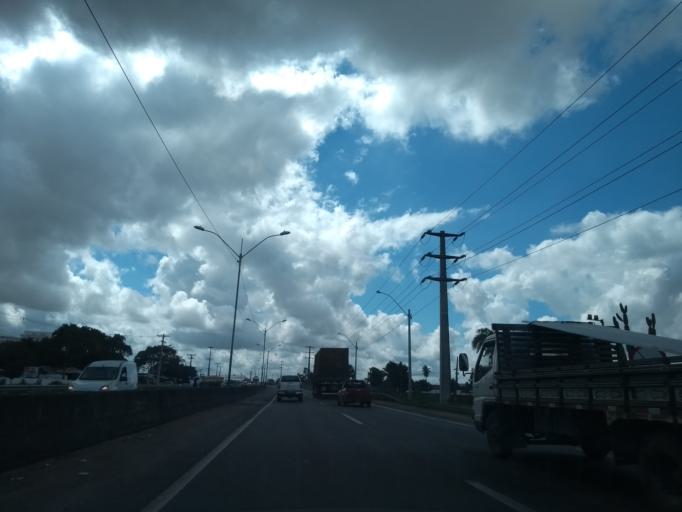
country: BR
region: Bahia
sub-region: Feira De Santana
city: Feira de Santana
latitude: -12.2787
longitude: -38.9409
